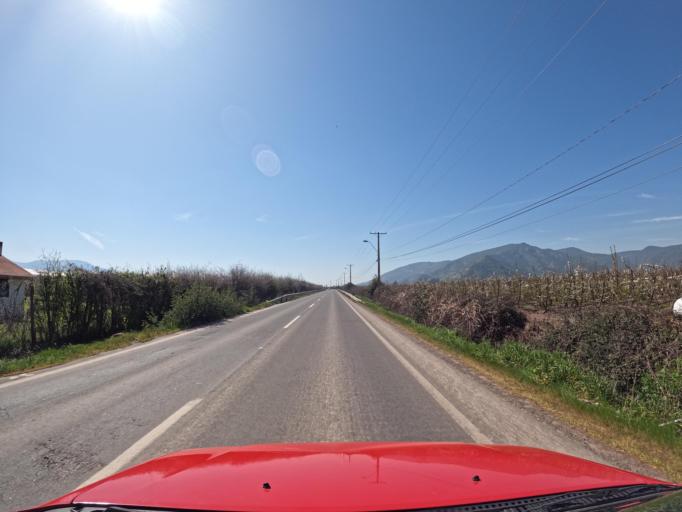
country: CL
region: Maule
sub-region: Provincia de Curico
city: Rauco
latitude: -35.0326
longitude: -71.4435
